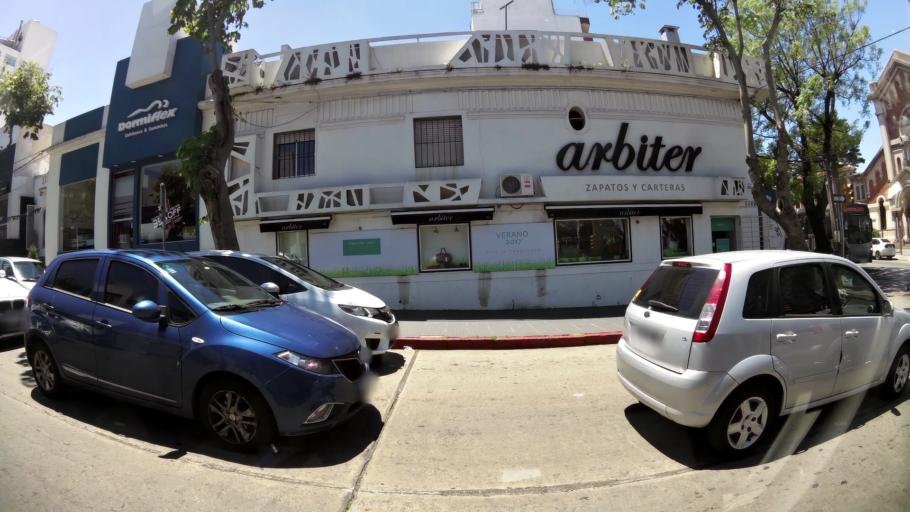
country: UY
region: Montevideo
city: Montevideo
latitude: -34.9228
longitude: -56.1593
